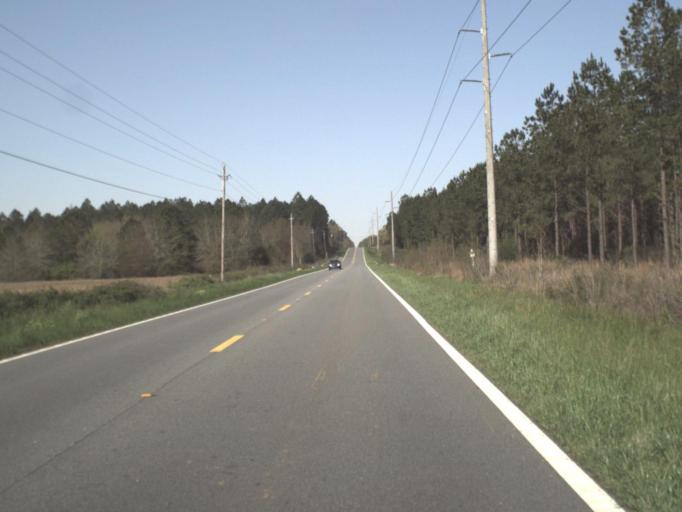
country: US
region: Florida
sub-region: Jackson County
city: Graceville
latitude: 30.9542
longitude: -85.4662
